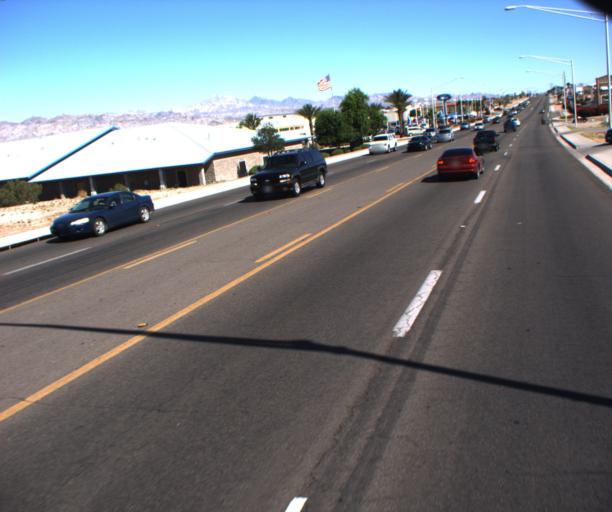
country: US
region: Arizona
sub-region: Mohave County
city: Bullhead City
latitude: 35.0901
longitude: -114.5980
